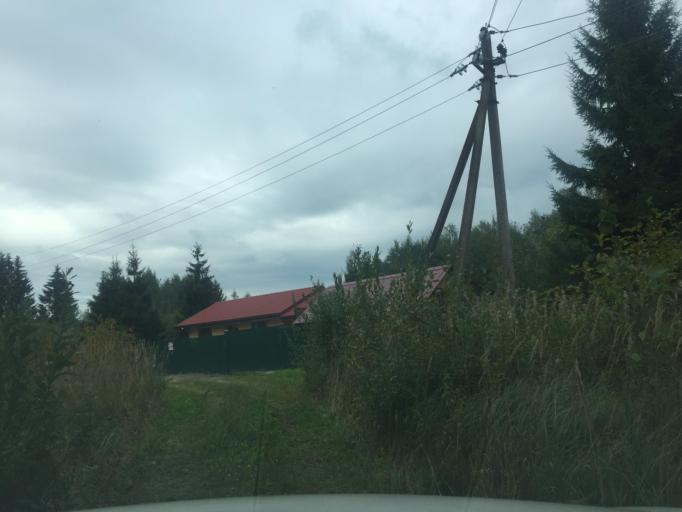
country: RU
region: Leningrad
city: Rozhdestveno
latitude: 59.2952
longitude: 30.0126
